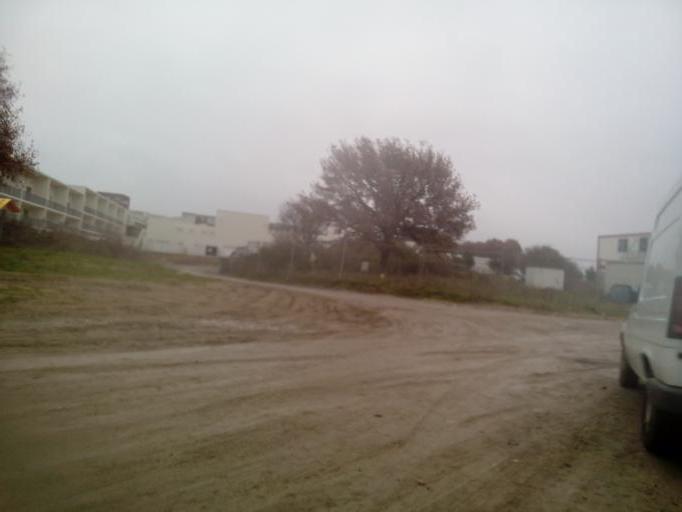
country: FR
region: Brittany
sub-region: Departement d'Ille-et-Vilaine
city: Saint-Jacques-de-la-Lande
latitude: 48.0769
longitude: -1.7193
